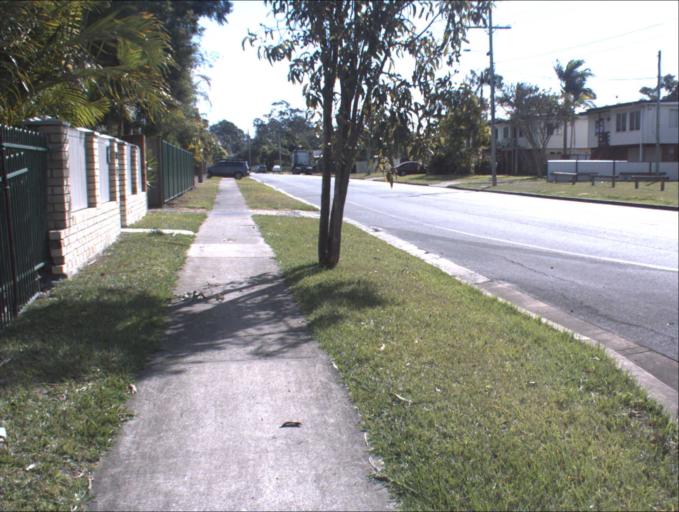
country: AU
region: Queensland
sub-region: Logan
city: Logan City
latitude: -27.6695
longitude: 153.1074
